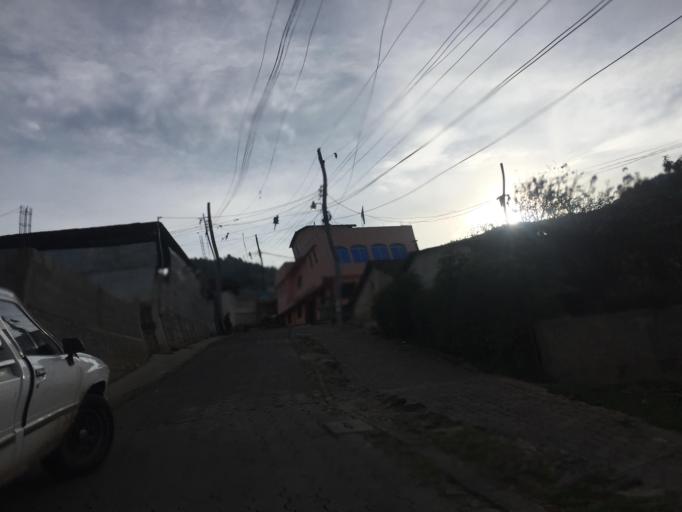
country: GT
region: Totonicapan
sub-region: Municipio de Totonicapan
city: Totonicapan
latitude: 14.9126
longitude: -91.3534
